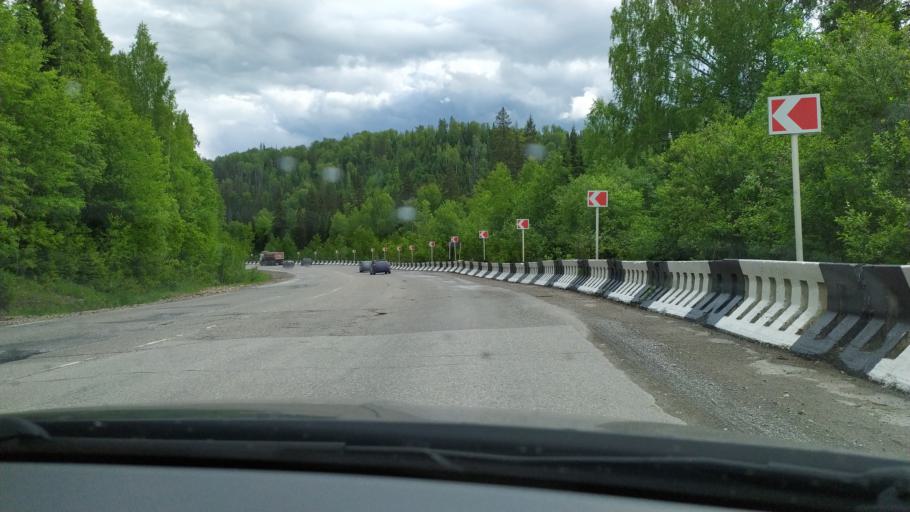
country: RU
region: Perm
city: Gremyachinsk
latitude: 58.4425
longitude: 57.8671
